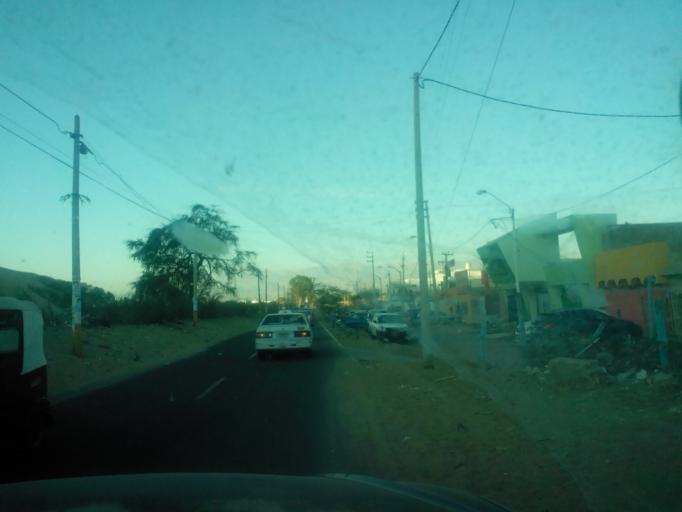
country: PE
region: Ica
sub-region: Provincia de Ica
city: Ica
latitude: -14.0860
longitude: -75.7564
